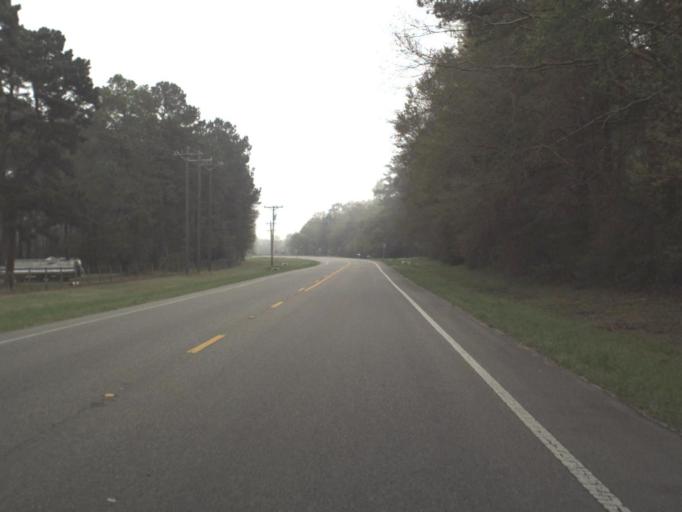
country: US
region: Florida
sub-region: Gadsden County
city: Gretna
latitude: 30.5660
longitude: -84.6750
